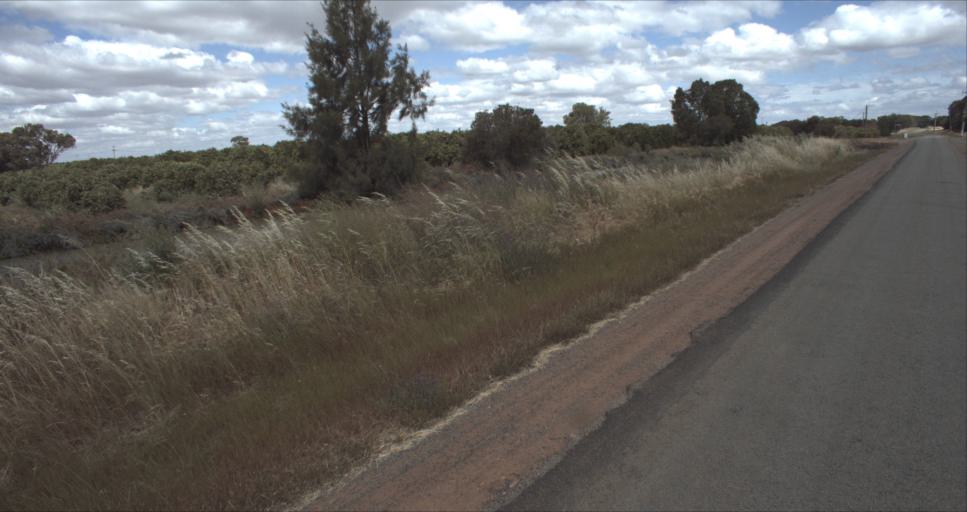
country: AU
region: New South Wales
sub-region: Leeton
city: Leeton
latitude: -34.5797
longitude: 146.3971
